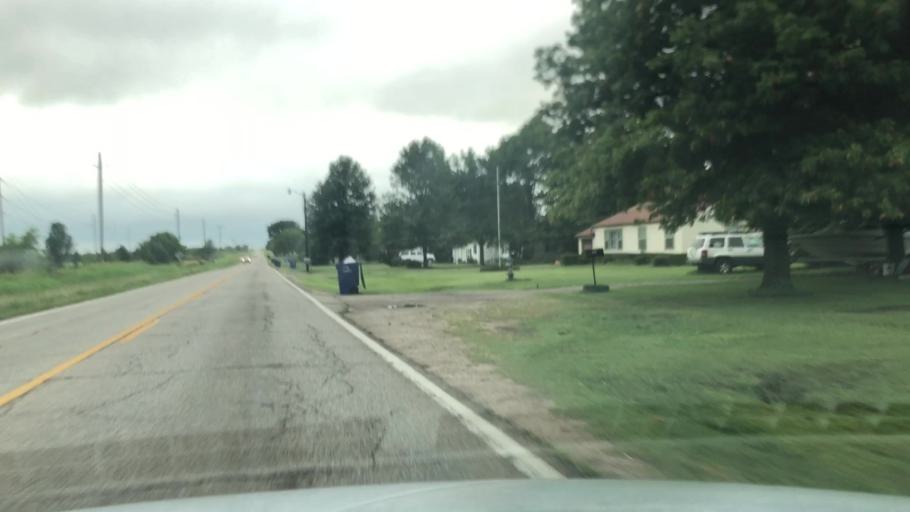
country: US
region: Oklahoma
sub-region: Nowata County
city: Nowata
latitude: 36.7039
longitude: -95.6500
